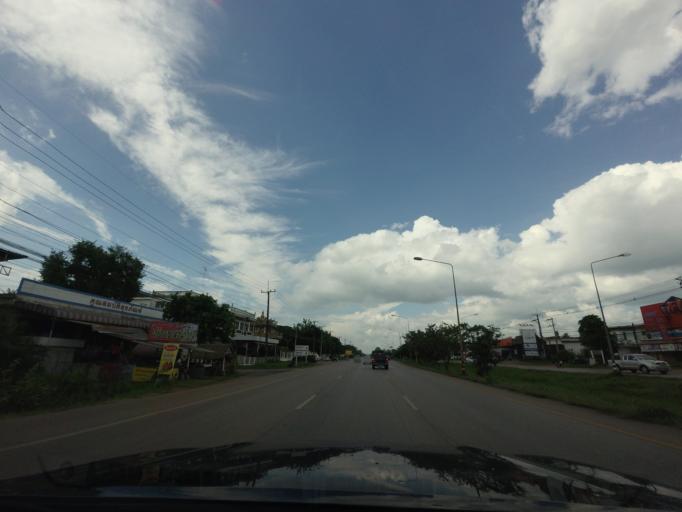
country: TH
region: Changwat Udon Thani
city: Udon Thani
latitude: 17.5348
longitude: 102.7999
